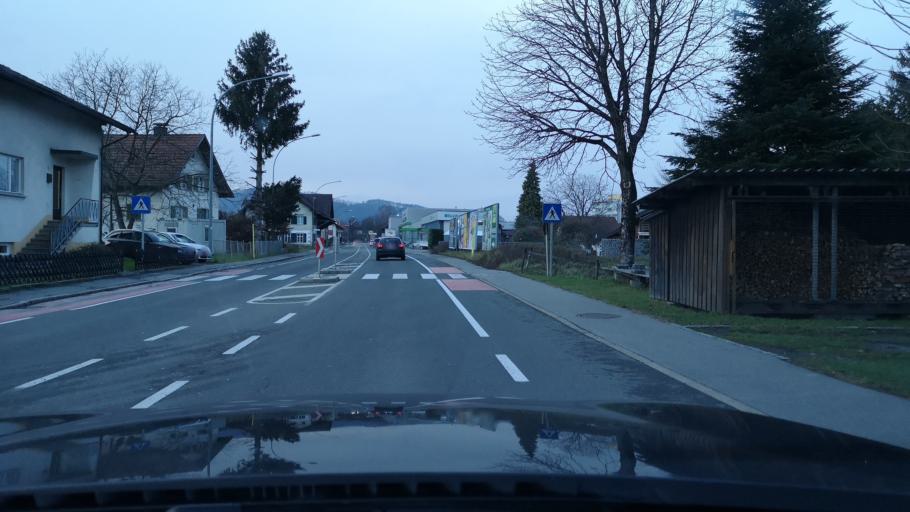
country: AT
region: Vorarlberg
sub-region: Politischer Bezirk Dornbirn
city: Lustenau
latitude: 47.4164
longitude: 9.6641
